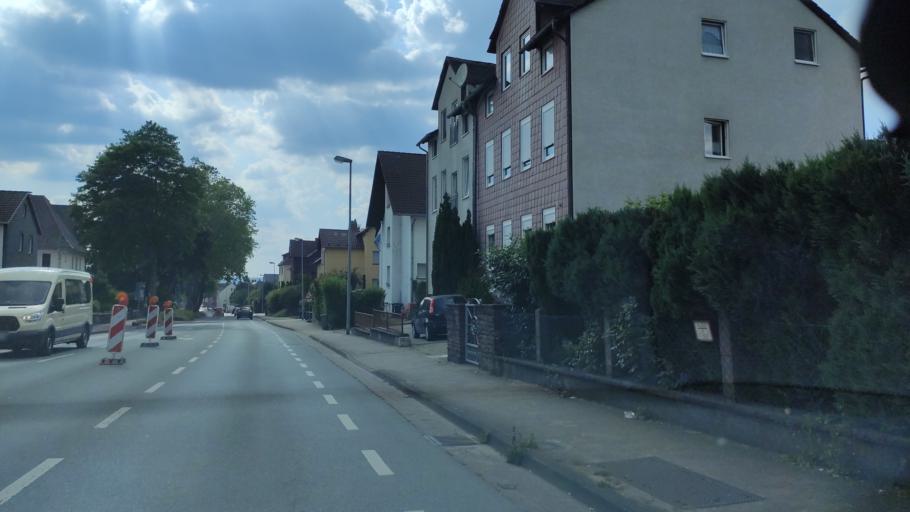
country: DE
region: Lower Saxony
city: Holzminden
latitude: 51.8281
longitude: 9.4670
